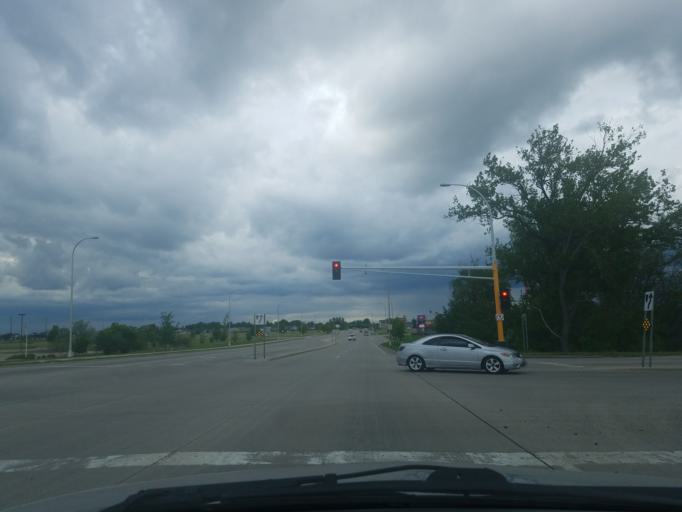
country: US
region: Minnesota
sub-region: Clay County
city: Dilworth
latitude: 46.8484
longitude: -96.7212
